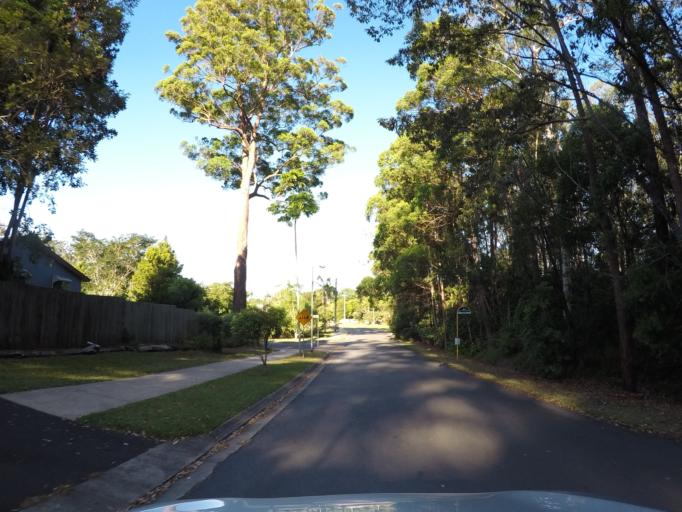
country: AU
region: Queensland
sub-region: Sunshine Coast
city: Nambour
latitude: -26.6212
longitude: 152.8603
